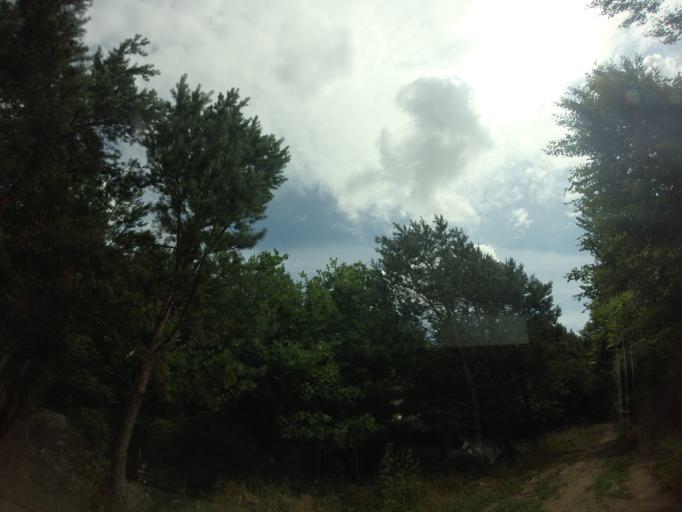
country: PL
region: West Pomeranian Voivodeship
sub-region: Powiat choszczenski
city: Drawno
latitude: 53.1975
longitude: 15.7703
